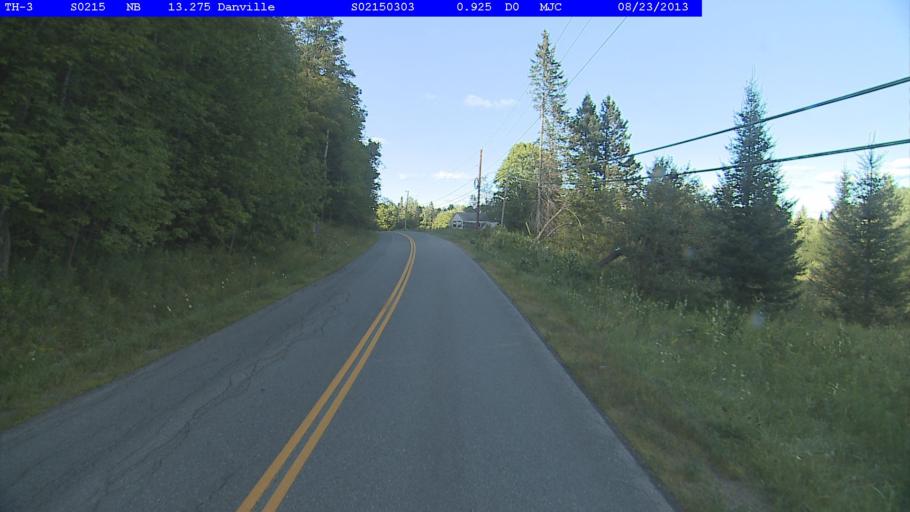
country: US
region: Vermont
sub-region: Caledonia County
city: Saint Johnsbury
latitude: 44.3788
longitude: -72.1439
